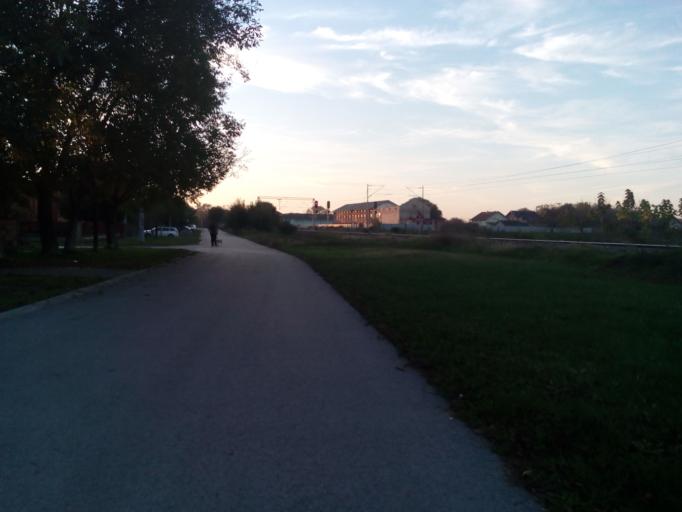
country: HR
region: Vukovarsko-Srijemska
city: Vinkovci
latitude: 45.3001
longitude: 18.8165
